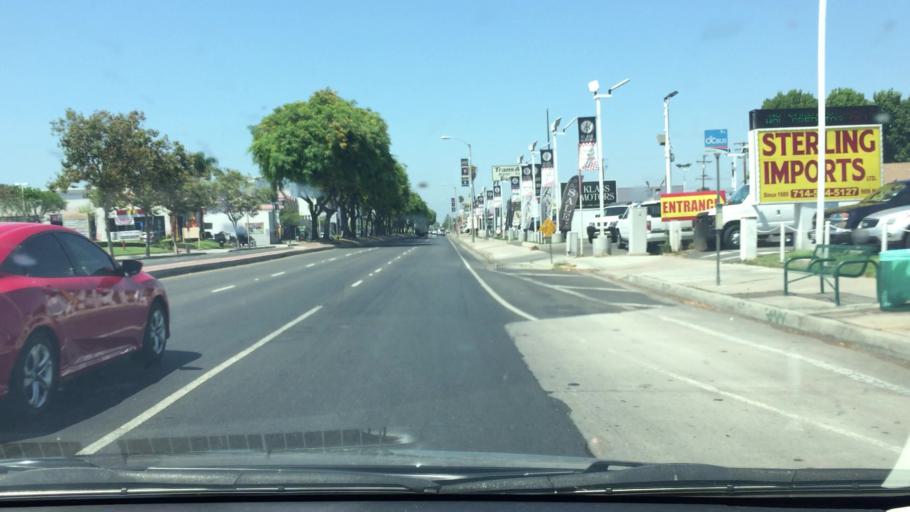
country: US
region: California
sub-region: Orange County
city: Garden Grove
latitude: 33.7527
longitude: -117.9201
